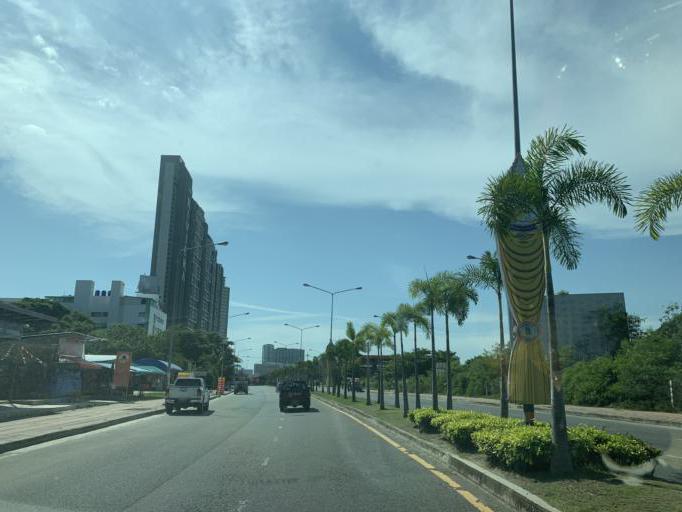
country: TH
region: Chon Buri
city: Phatthaya
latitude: 12.8803
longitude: 100.8884
